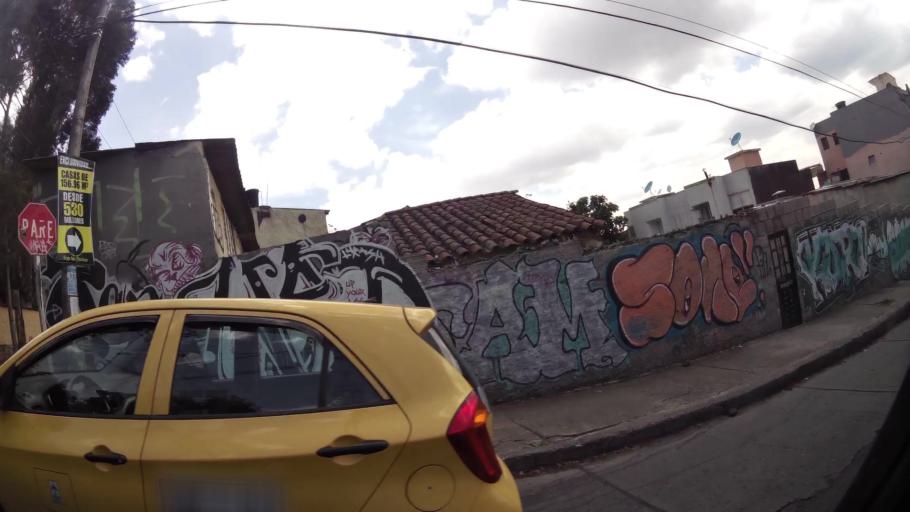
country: CO
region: Cundinamarca
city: Cota
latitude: 4.7443
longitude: -74.0831
